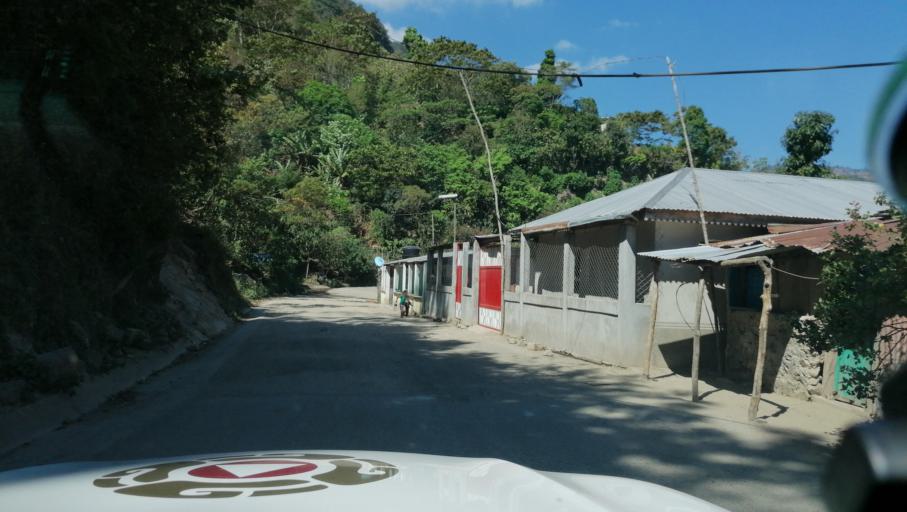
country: GT
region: San Marcos
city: Tacana
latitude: 15.1928
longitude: -92.1852
